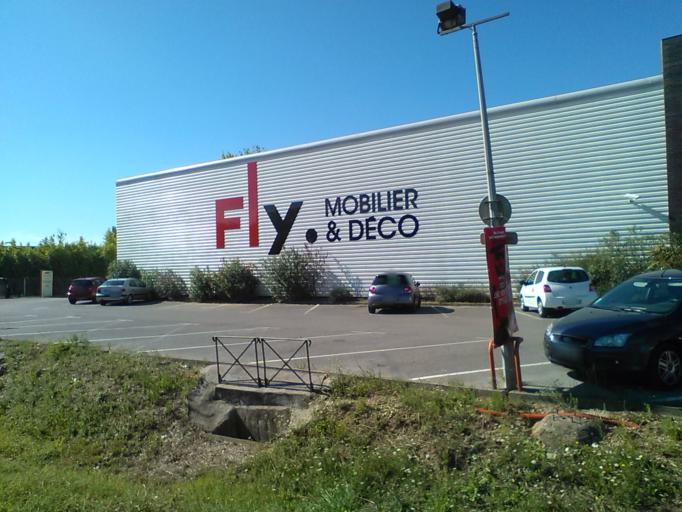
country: FR
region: Languedoc-Roussillon
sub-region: Departement de l'Herault
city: Perols
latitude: 43.5757
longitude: 3.9395
